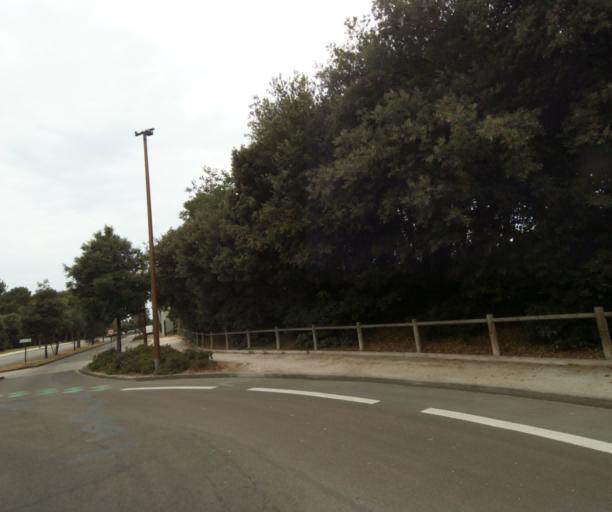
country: FR
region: Pays de la Loire
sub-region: Departement de la Vendee
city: Chateau-d'Olonne
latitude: 46.4850
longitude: -1.7556
